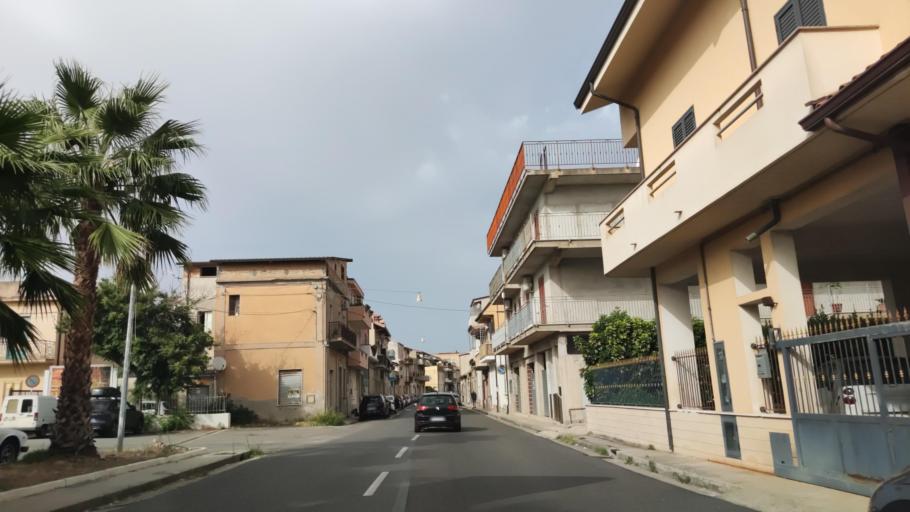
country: IT
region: Calabria
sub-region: Provincia di Reggio Calabria
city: Siderno
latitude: 38.2609
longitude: 16.2883
